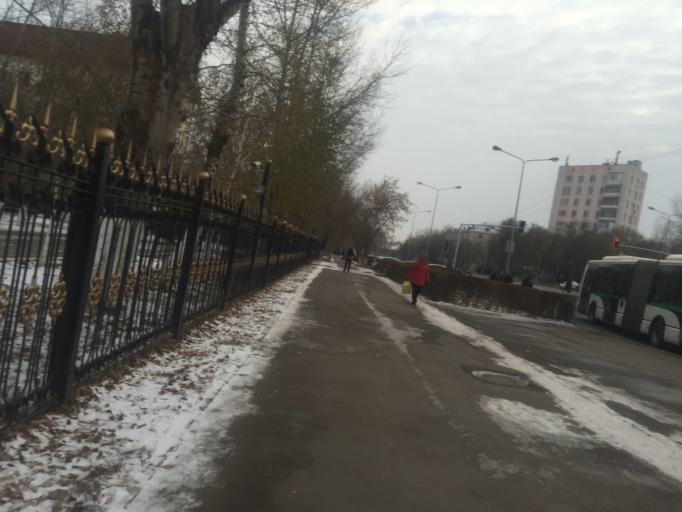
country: KZ
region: Astana Qalasy
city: Astana
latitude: 51.1800
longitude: 71.4103
